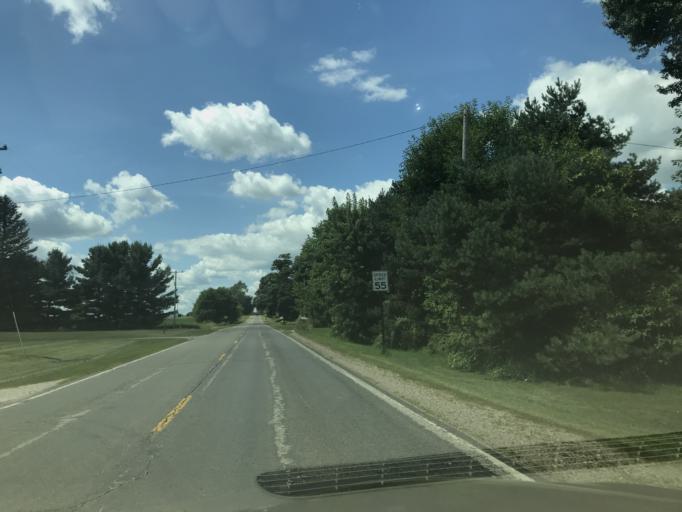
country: US
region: Michigan
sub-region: Ingham County
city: Leslie
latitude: 42.4512
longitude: -84.4493
